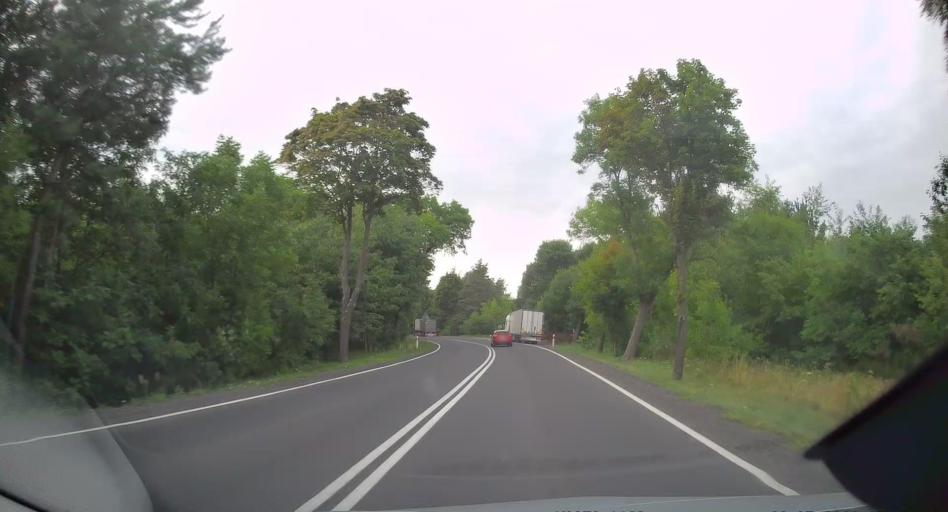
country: PL
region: Lodz Voivodeship
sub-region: Powiat radomszczanski
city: Gomunice
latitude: 51.1808
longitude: 19.4958
